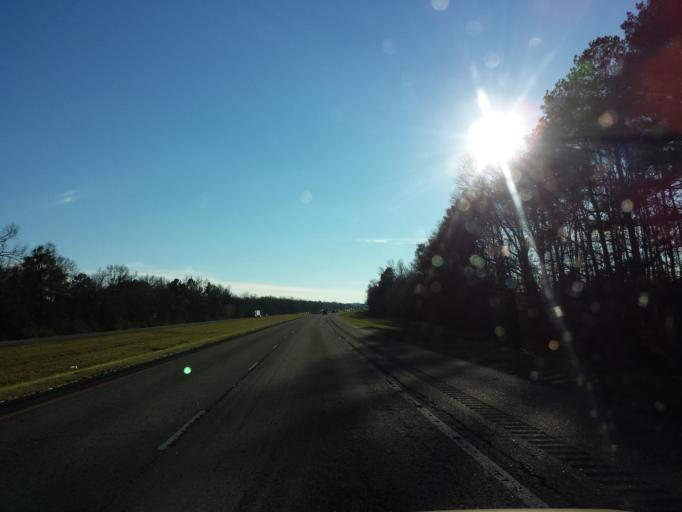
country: US
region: Alabama
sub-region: Hale County
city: Moundville
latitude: 33.1098
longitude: -87.6579
